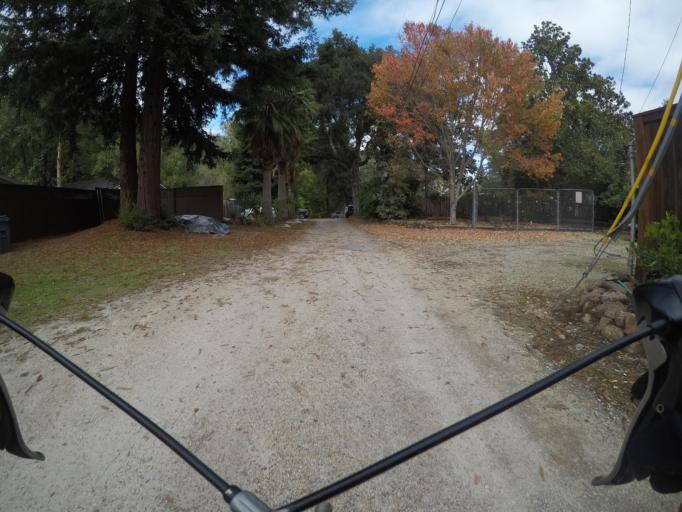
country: US
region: California
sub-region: Santa Cruz County
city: Ben Lomond
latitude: 37.0750
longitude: -122.0820
